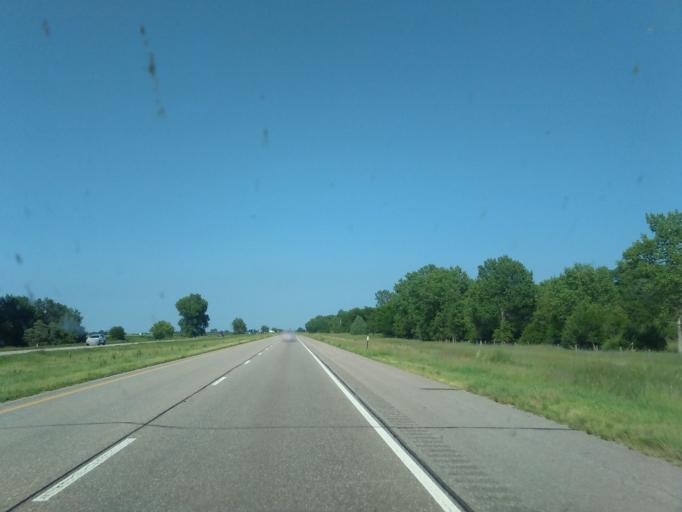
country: US
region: Nebraska
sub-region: Hall County
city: Wood River
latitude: 40.7760
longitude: -98.5484
